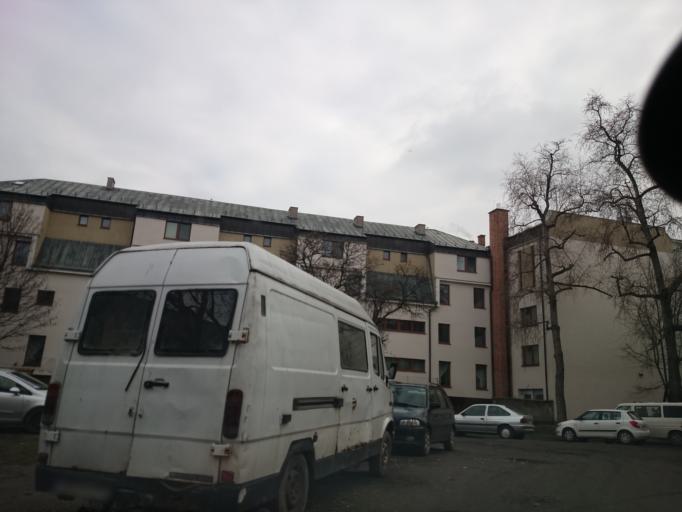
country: PL
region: Opole Voivodeship
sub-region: Powiat opolski
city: Opole
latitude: 50.6726
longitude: 17.9199
